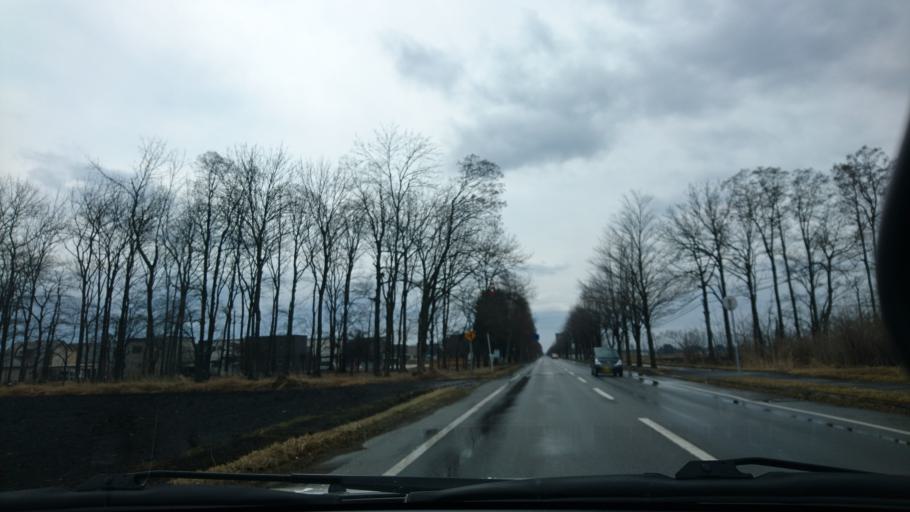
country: JP
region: Hokkaido
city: Otofuke
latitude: 43.0049
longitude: 143.1875
